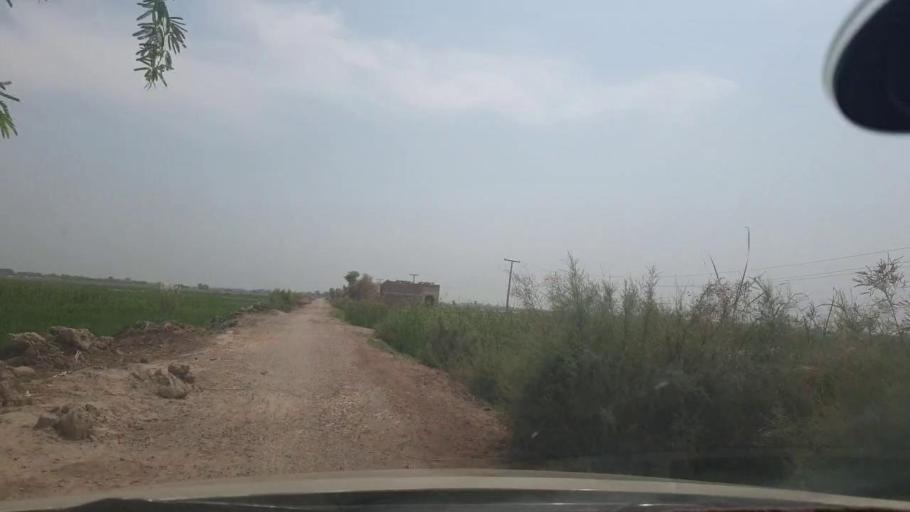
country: PK
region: Sindh
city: Jacobabad
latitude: 28.2316
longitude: 68.3889
